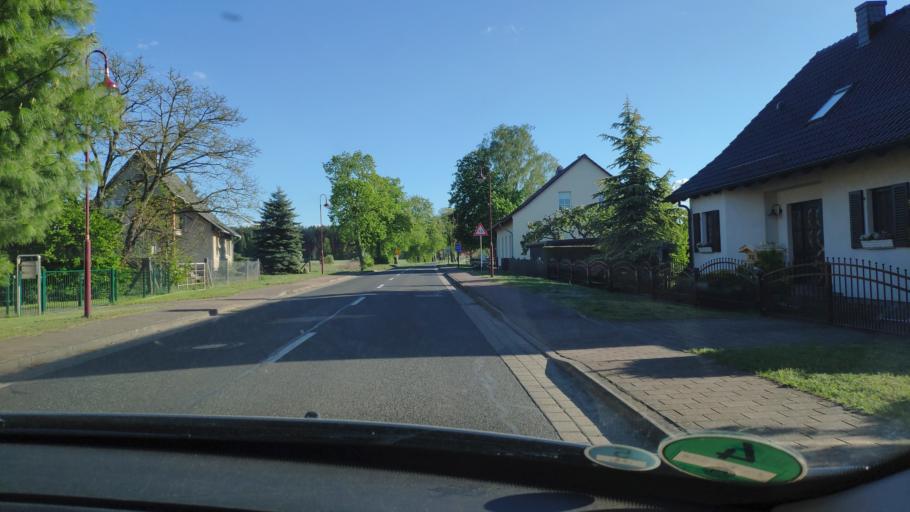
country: DE
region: Mecklenburg-Vorpommern
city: Wesenberg
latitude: 53.3375
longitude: 12.9807
